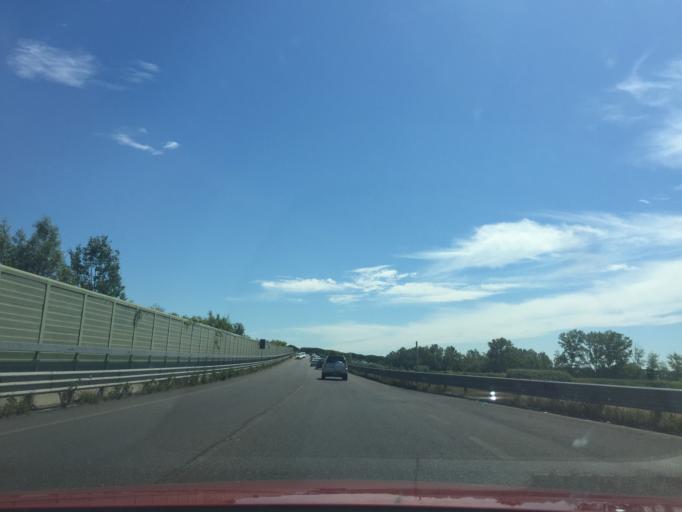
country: IT
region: Tuscany
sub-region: Province of Pisa
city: Pontedera
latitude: 43.6765
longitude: 10.6349
